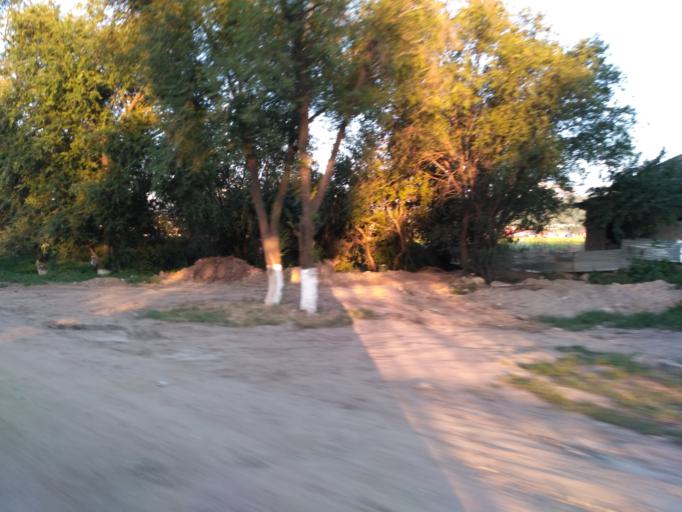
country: KZ
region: Almaty Qalasy
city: Almaty
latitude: 43.1744
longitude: 76.7851
